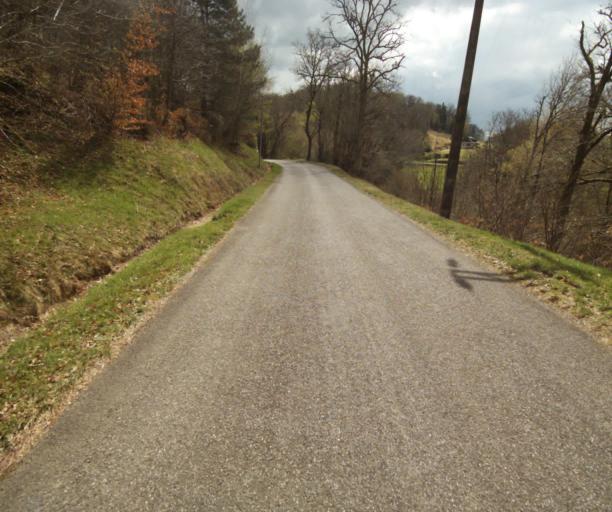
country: FR
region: Limousin
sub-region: Departement de la Correze
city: Laguenne
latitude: 45.2406
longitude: 1.8894
